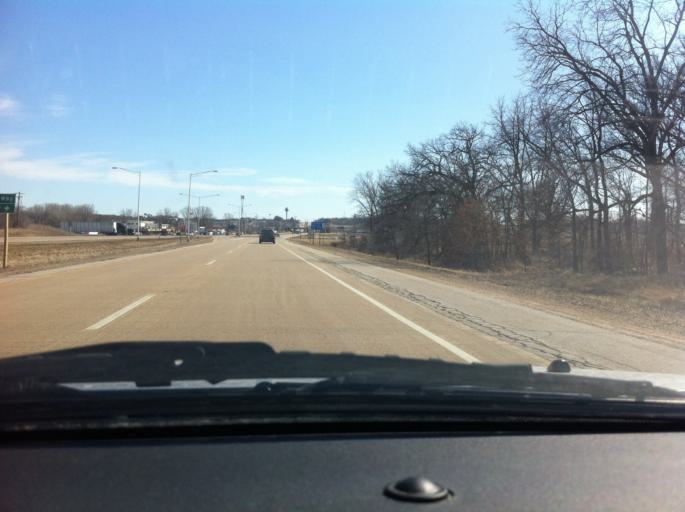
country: US
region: Wisconsin
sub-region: Dane County
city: Windsor
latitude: 43.1884
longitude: -89.3246
